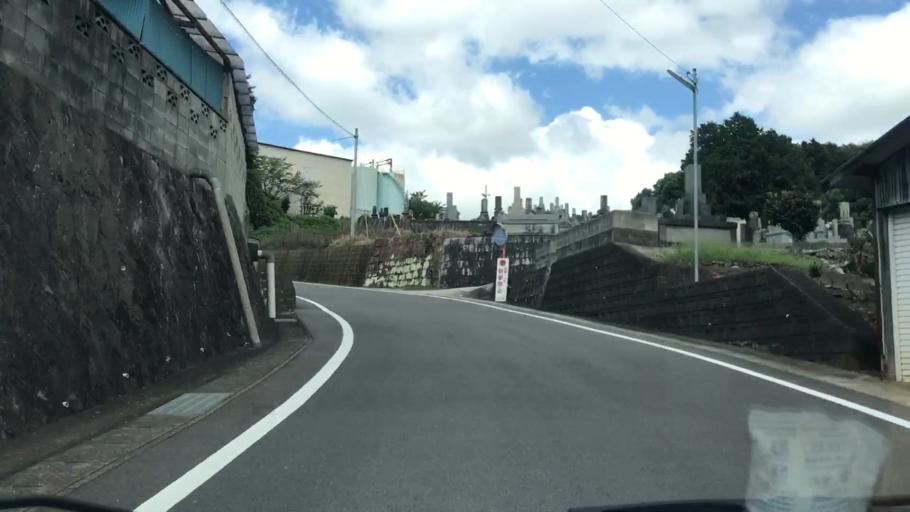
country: JP
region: Saga Prefecture
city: Takeocho-takeo
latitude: 33.2286
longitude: 130.1428
